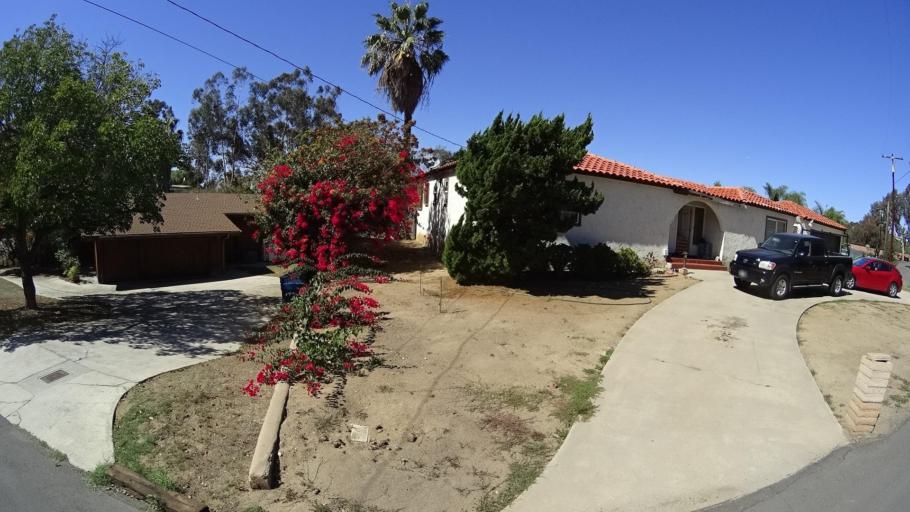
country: US
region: California
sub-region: San Diego County
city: Bonita
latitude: 32.6661
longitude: -117.0469
